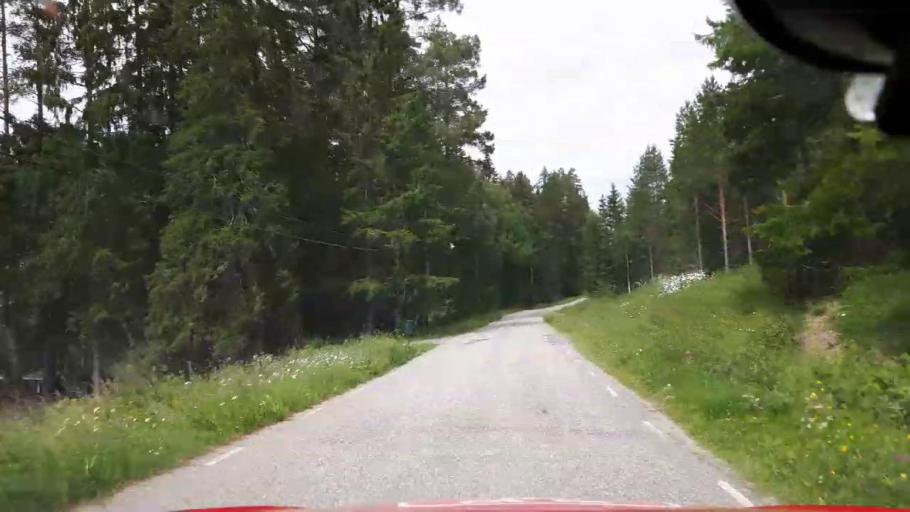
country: SE
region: Jaemtland
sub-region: Braecke Kommun
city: Braecke
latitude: 62.8624
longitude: 15.2745
